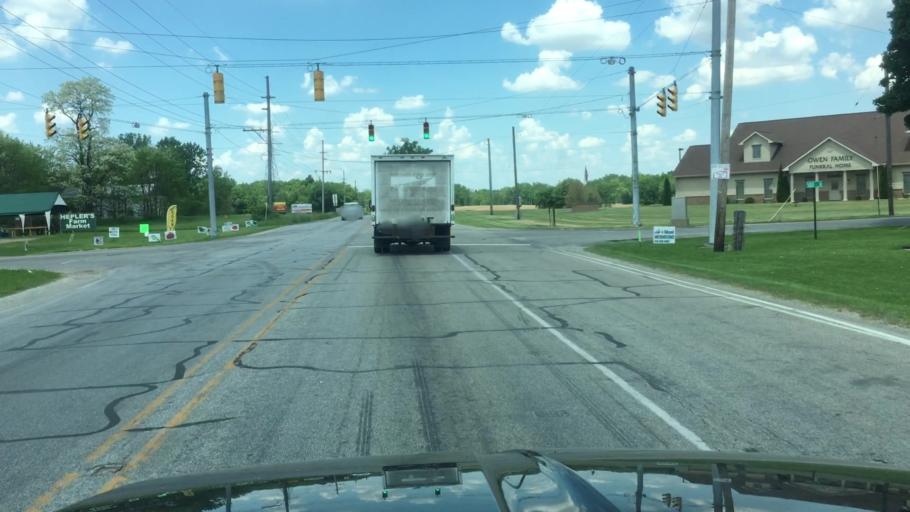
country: US
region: Indiana
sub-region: Kosciusko County
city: North Webster
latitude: 41.3085
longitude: -85.6910
